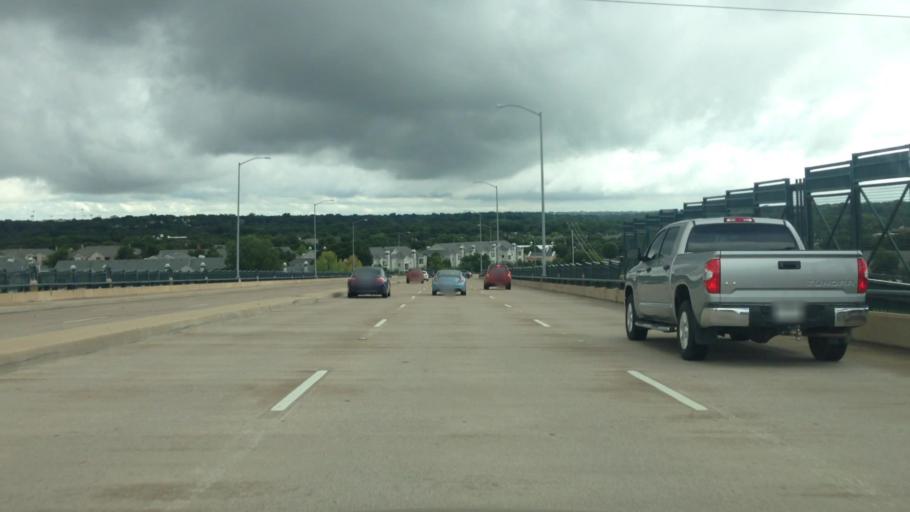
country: US
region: Texas
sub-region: Tarrant County
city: Westworth
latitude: 32.7177
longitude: -97.3857
